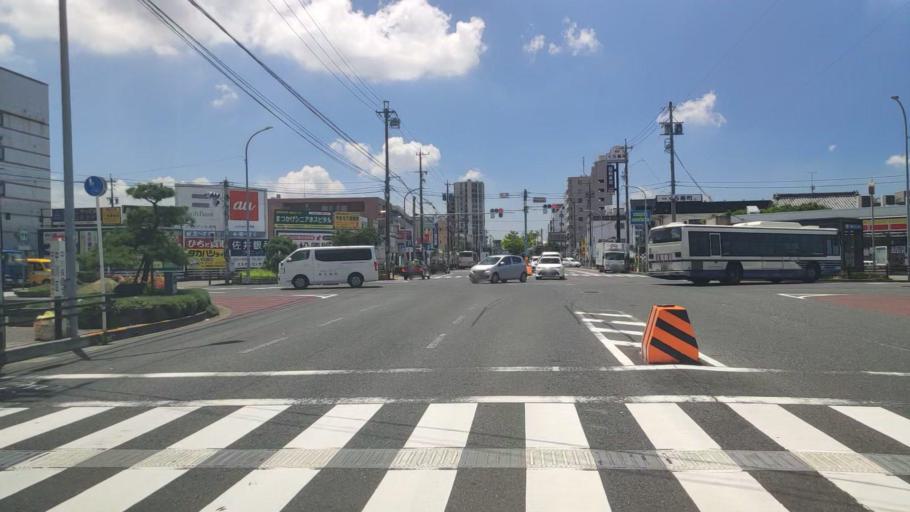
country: JP
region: Aichi
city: Kanie
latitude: 35.1405
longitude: 136.8532
